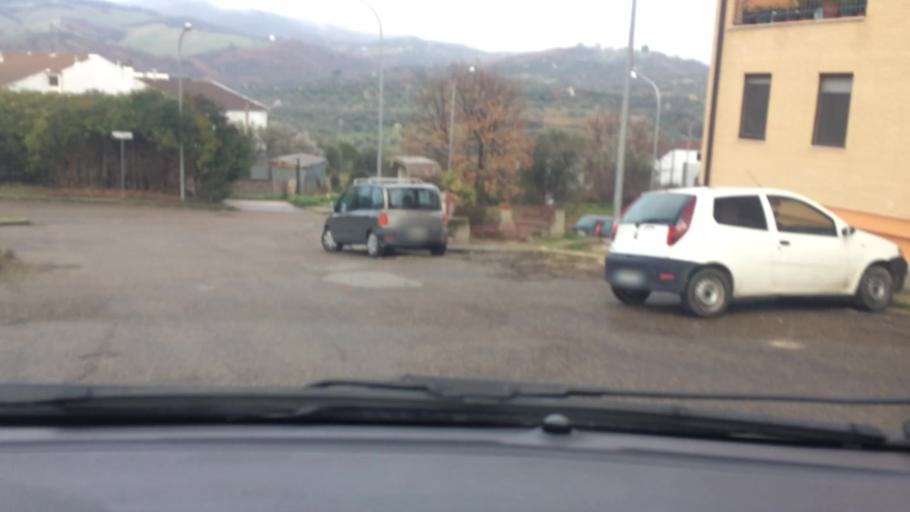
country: IT
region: Basilicate
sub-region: Provincia di Matera
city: San Mauro Forte
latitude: 40.4898
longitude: 16.2425
